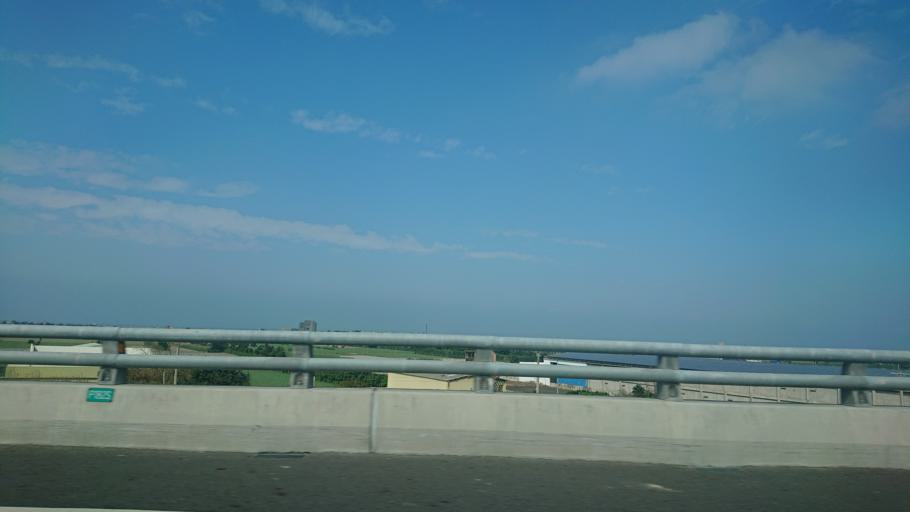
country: TW
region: Taiwan
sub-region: Changhua
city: Chang-hua
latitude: 23.9932
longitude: 120.3759
